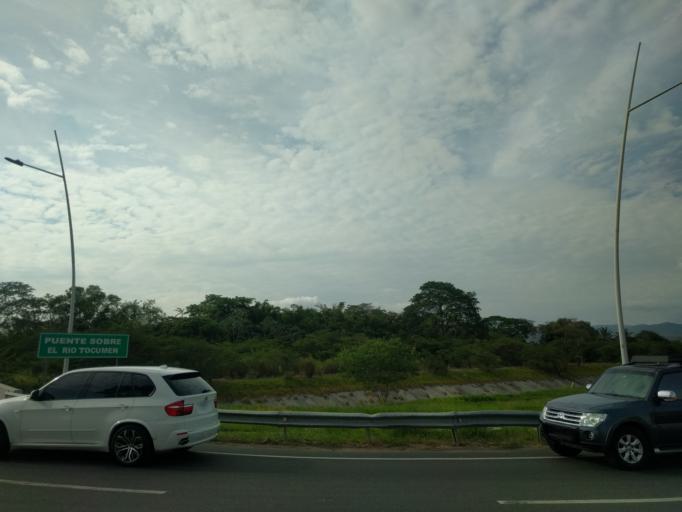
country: PA
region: Panama
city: Tocumen
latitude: 9.0627
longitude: -79.3935
